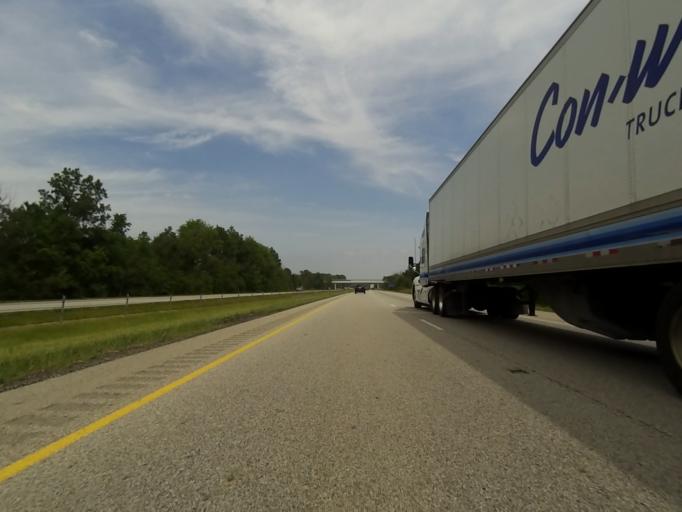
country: US
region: Ohio
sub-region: Portage County
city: Ravenna
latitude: 41.1060
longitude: -81.1263
